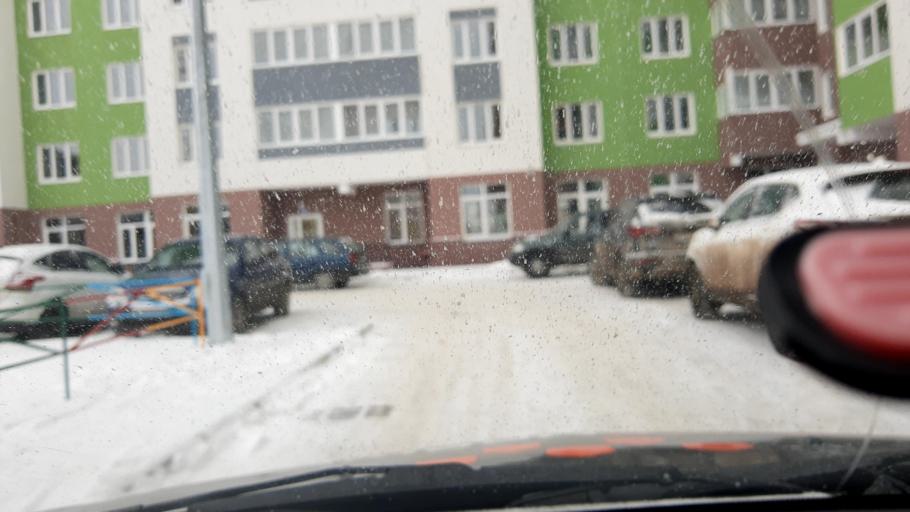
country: RU
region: Bashkortostan
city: Avdon
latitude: 54.7102
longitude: 55.8102
